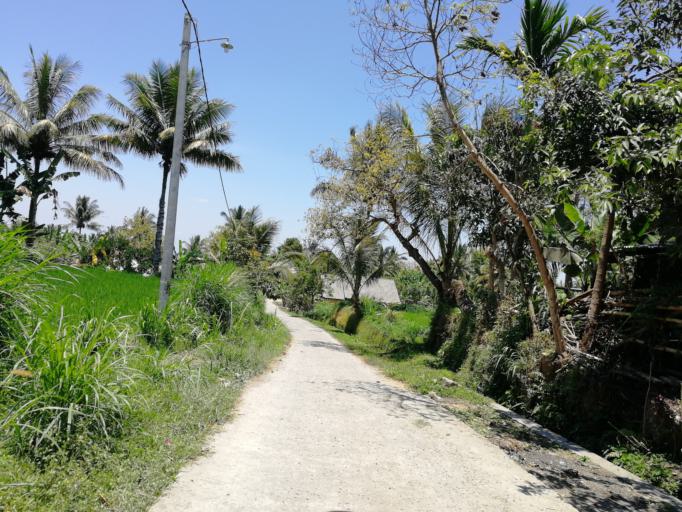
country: ID
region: West Nusa Tenggara
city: Tetebatu
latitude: -8.5445
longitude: 116.4211
